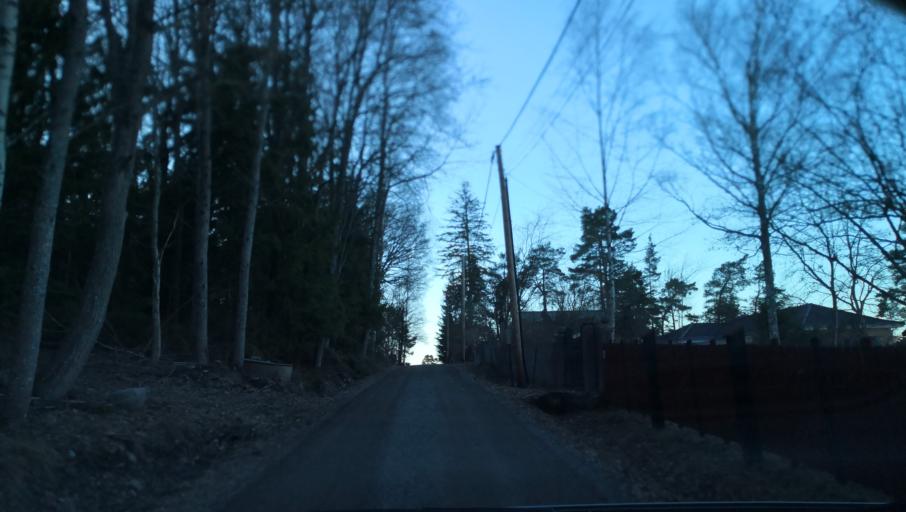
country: SE
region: Stockholm
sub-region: Varmdo Kommun
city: Mortnas
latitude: 59.3349
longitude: 18.4497
